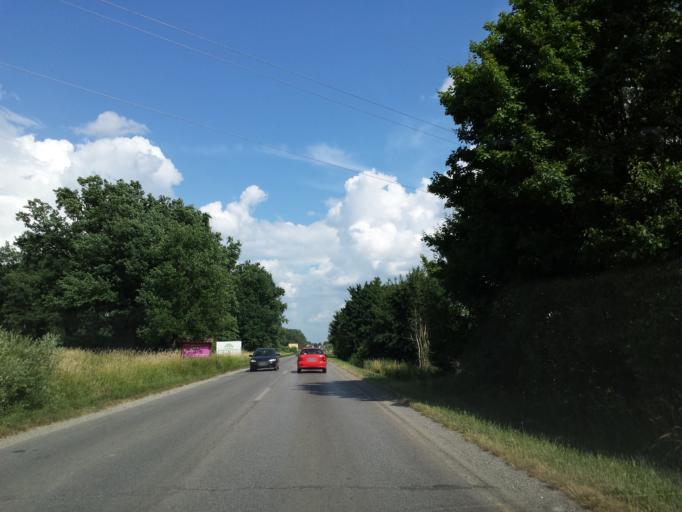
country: HR
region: Grad Zagreb
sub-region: Sesvete
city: Sesvete
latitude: 45.8130
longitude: 16.1911
